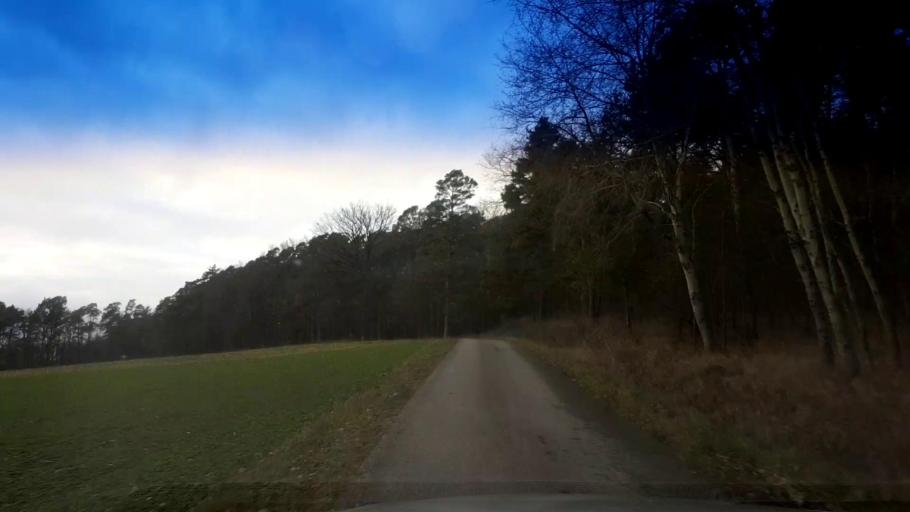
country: DE
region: Bavaria
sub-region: Upper Franconia
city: Lauter
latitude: 49.9560
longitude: 10.7641
